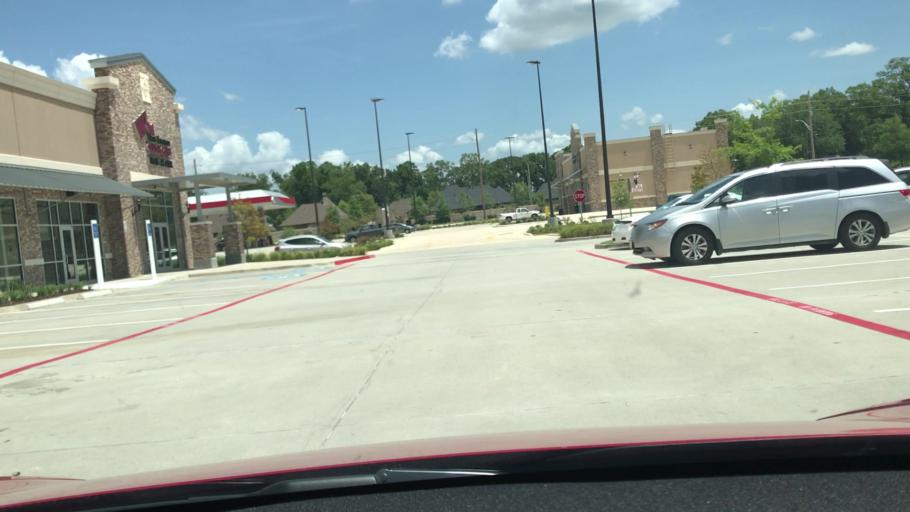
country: US
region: Louisiana
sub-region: Bossier Parish
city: Bossier City
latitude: 32.3951
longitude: -93.7288
